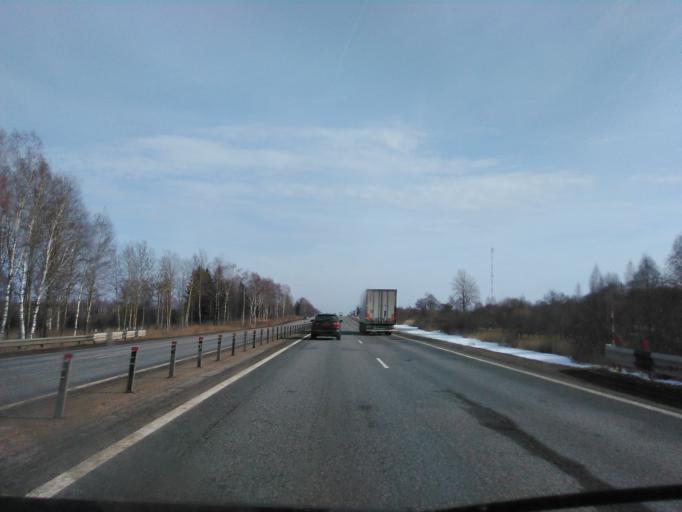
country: BY
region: Vitebsk
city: Dubrowna
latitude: 54.6880
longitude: 30.8642
